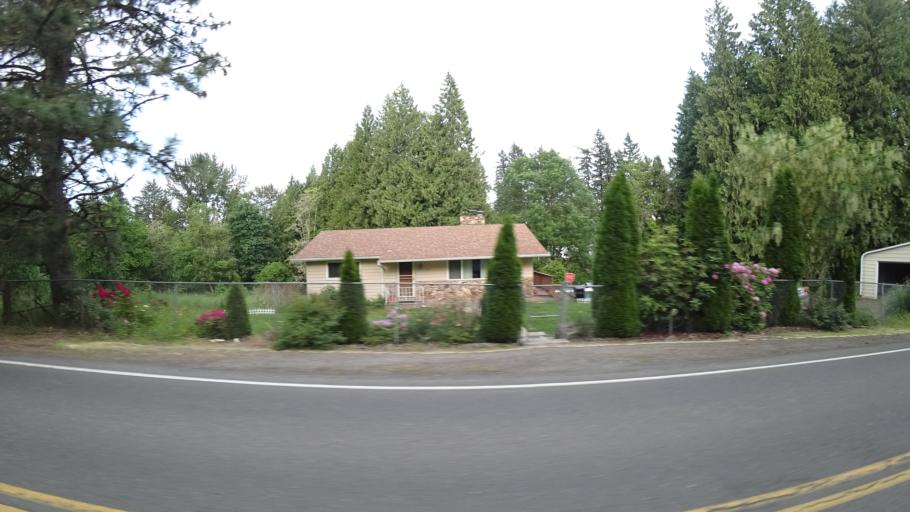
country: US
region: Oregon
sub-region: Clackamas County
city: Happy Valley
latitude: 45.4698
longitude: -122.4967
